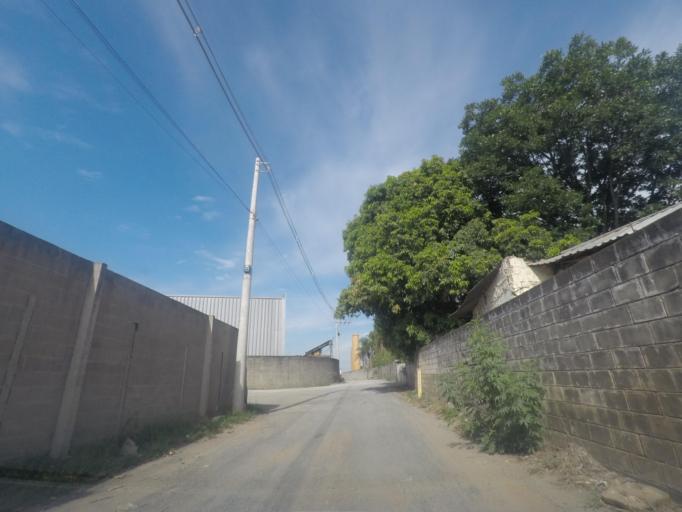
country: BR
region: Sao Paulo
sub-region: Sumare
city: Sumare
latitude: -22.7849
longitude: -47.2310
